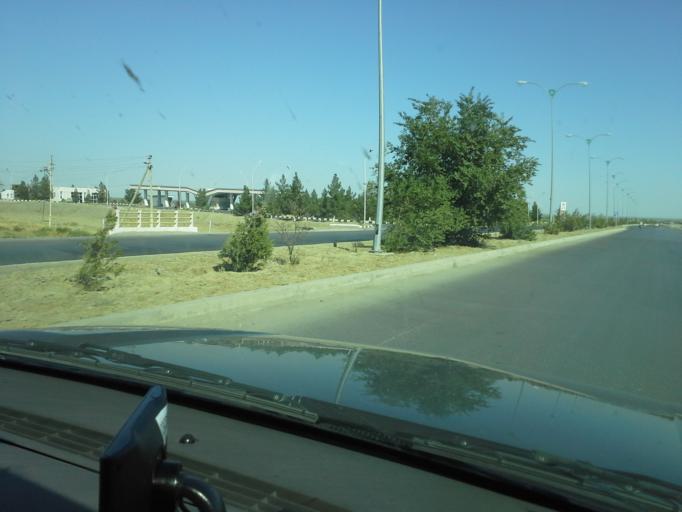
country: TM
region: Ahal
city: Baharly
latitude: 38.4170
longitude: 57.4462
